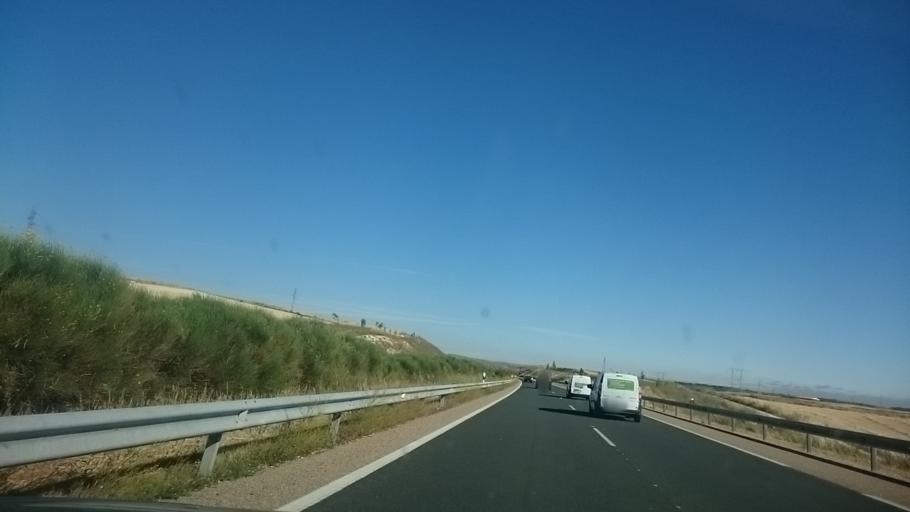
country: ES
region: Castille and Leon
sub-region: Provincia de Burgos
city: Villalbilla de Burgos
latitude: 42.3234
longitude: -3.7677
